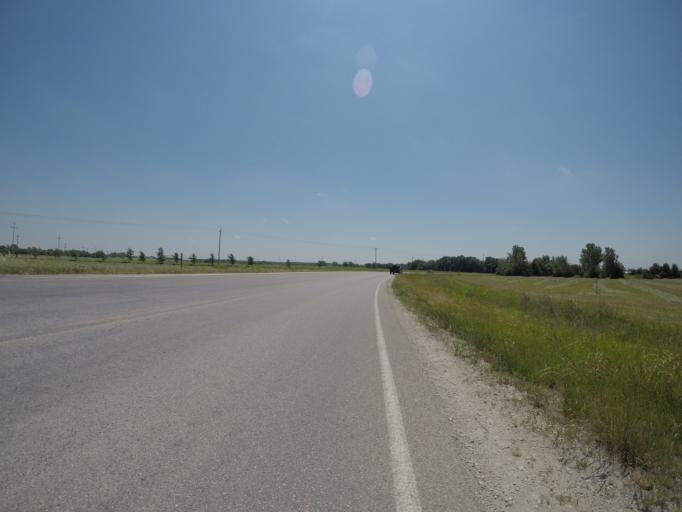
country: US
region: Kansas
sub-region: Riley County
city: Manhattan
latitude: 39.2320
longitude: -96.4417
